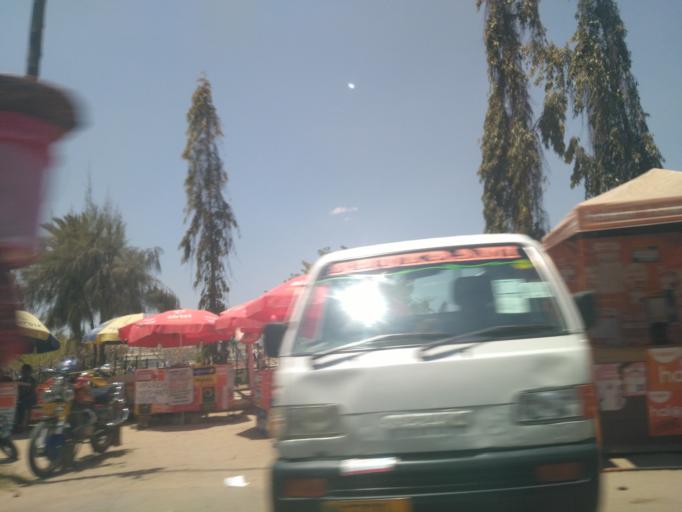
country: TZ
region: Dodoma
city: Dodoma
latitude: -6.1795
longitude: 35.7474
